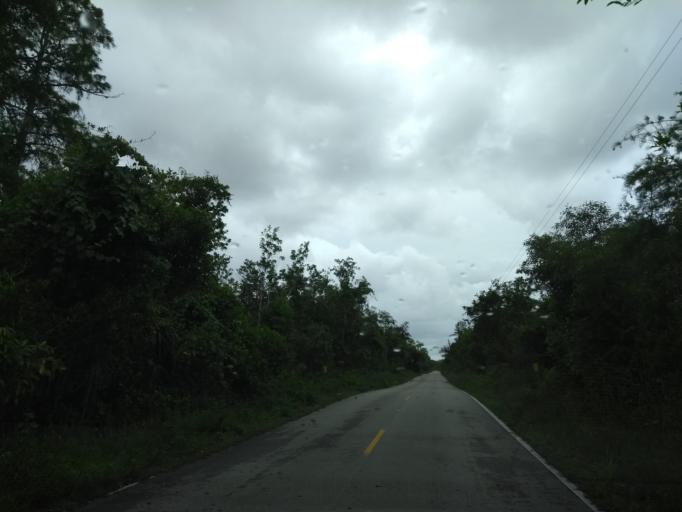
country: US
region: Florida
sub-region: Miami-Dade County
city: The Hammocks
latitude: 25.7596
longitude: -80.9256
